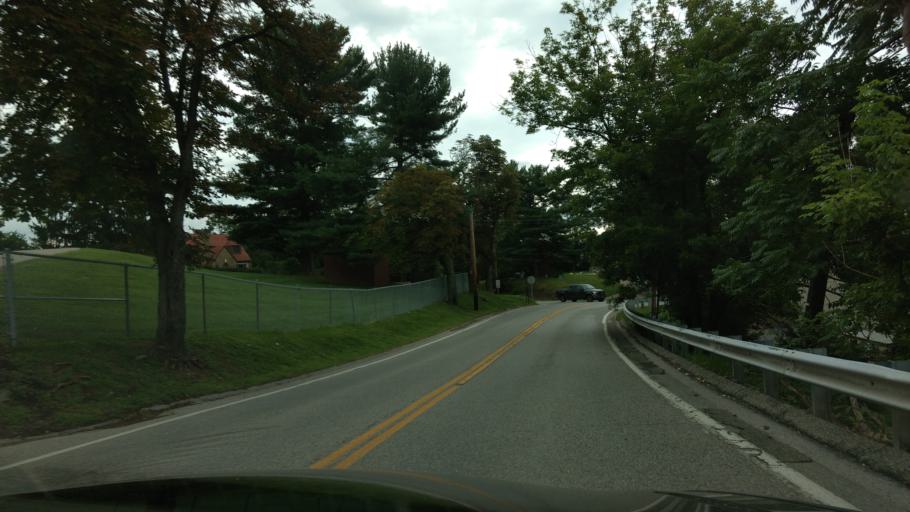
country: US
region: Pennsylvania
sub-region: Allegheny County
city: Bellevue
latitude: 40.5069
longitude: -80.0485
